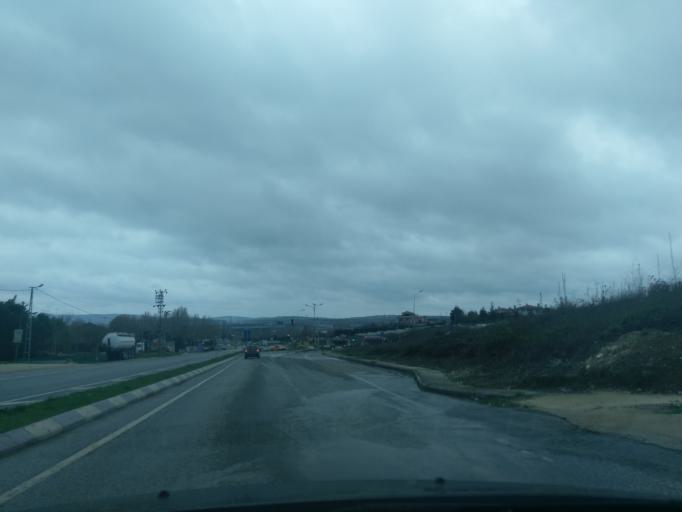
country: TR
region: Istanbul
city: Catalca
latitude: 41.1583
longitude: 28.4538
